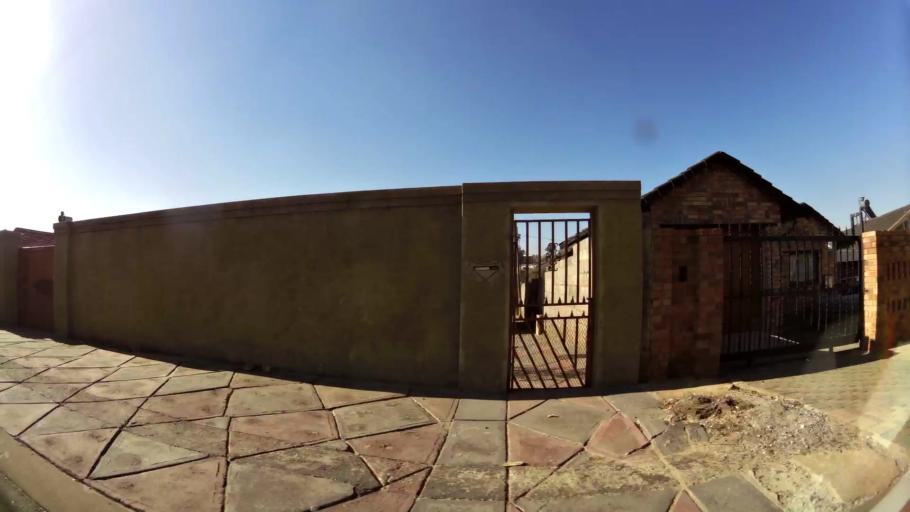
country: ZA
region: Gauteng
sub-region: City of Johannesburg Metropolitan Municipality
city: Soweto
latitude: -26.2312
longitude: 27.9178
